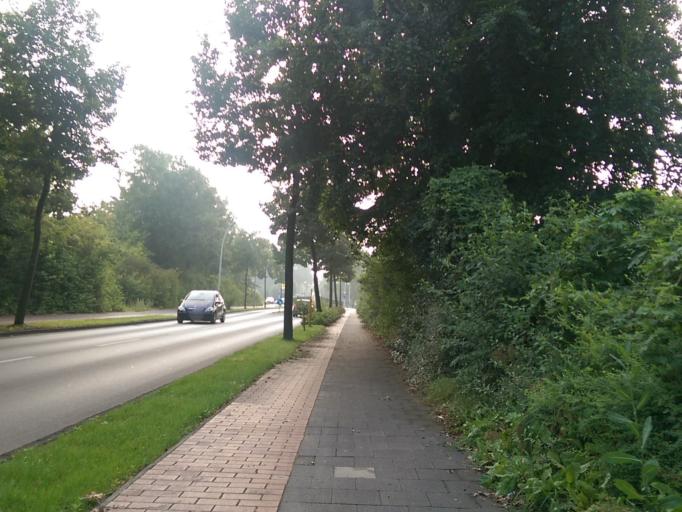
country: DE
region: North Rhine-Westphalia
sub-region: Regierungsbezirk Detmold
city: Harsewinkel
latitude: 51.9650
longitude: 8.2419
